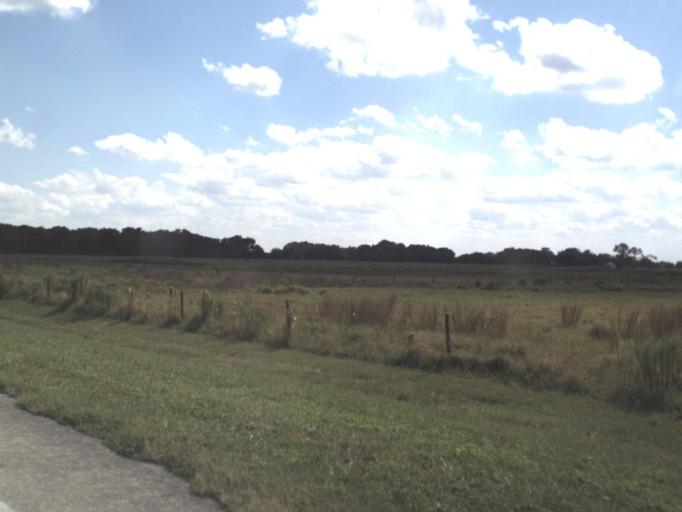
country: US
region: Florida
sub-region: Highlands County
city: Sebring
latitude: 27.4288
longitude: -81.5886
